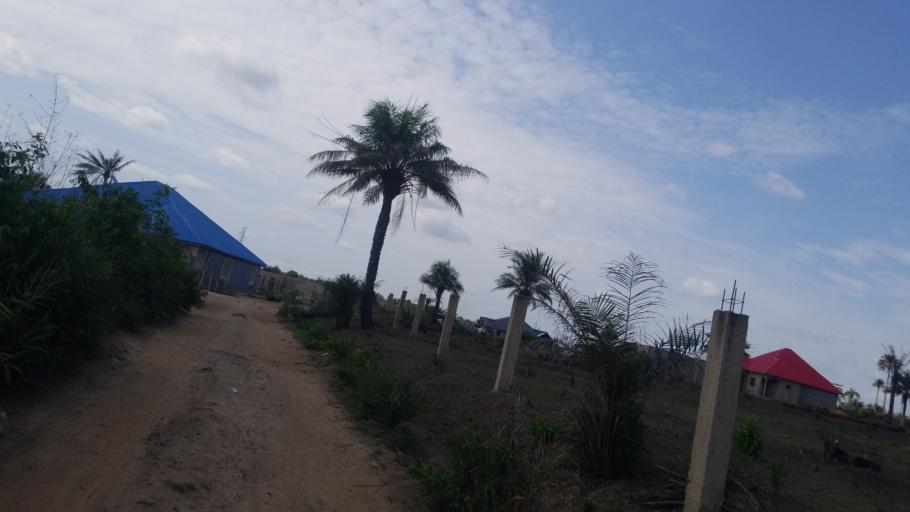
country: SL
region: Western Area
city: Waterloo
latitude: 8.3267
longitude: -13.0246
